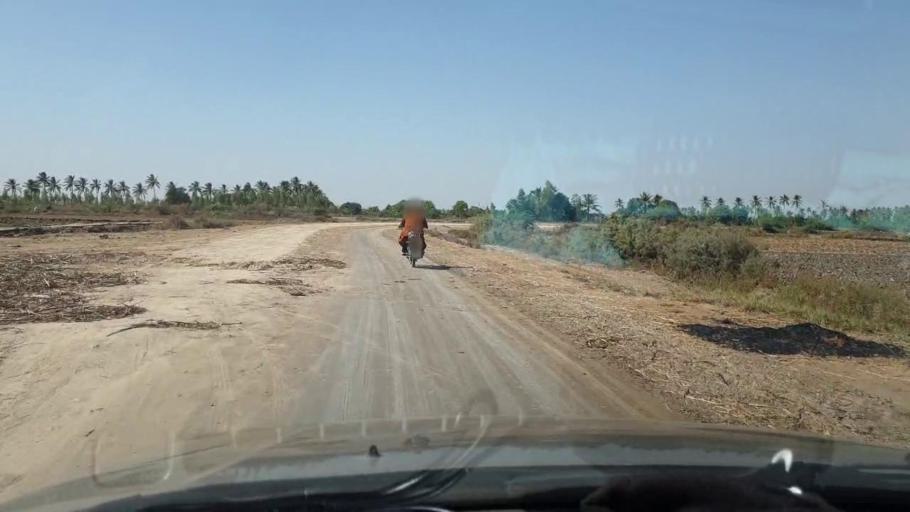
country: PK
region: Sindh
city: Thatta
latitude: 24.6340
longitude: 67.8959
